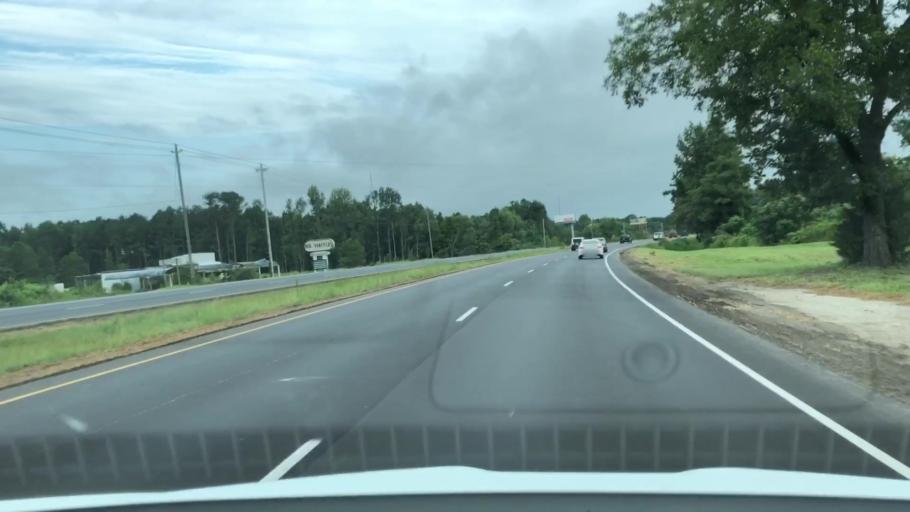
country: US
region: North Carolina
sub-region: Lenoir County
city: Kinston
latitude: 35.2467
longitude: -77.5915
